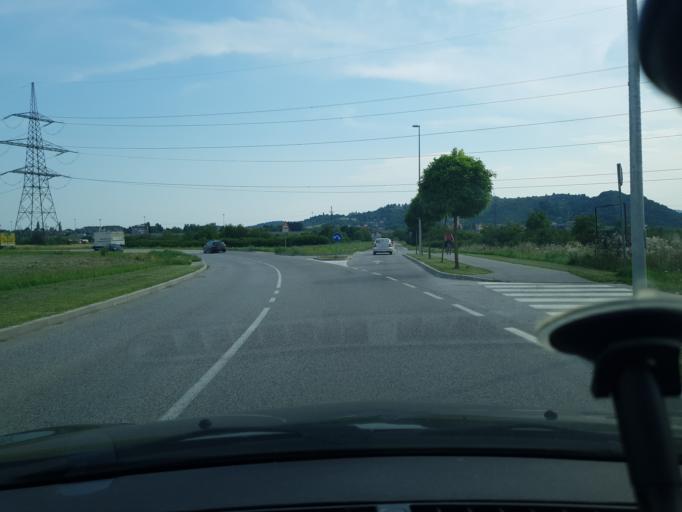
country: HR
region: Zagrebacka
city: Bestovje
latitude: 45.8043
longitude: 15.7848
